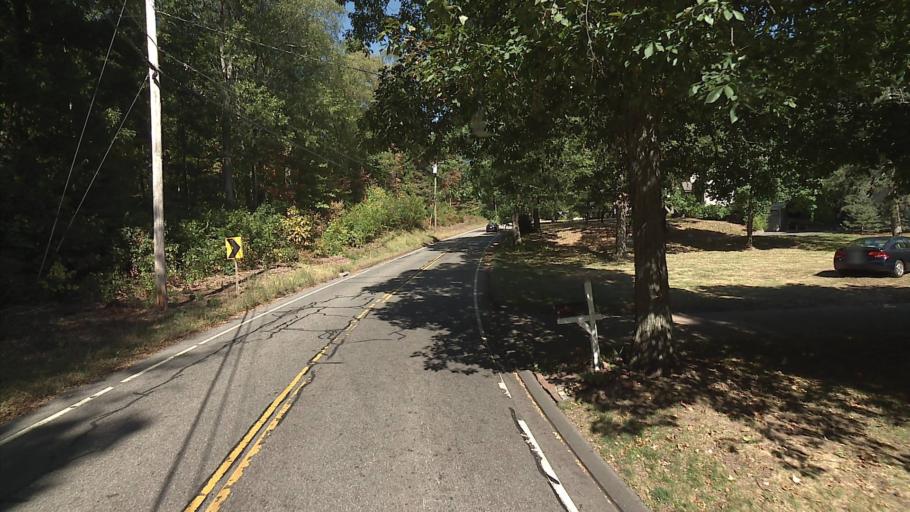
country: US
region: Connecticut
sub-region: Hartford County
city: Manchester
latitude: 41.7192
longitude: -72.5269
